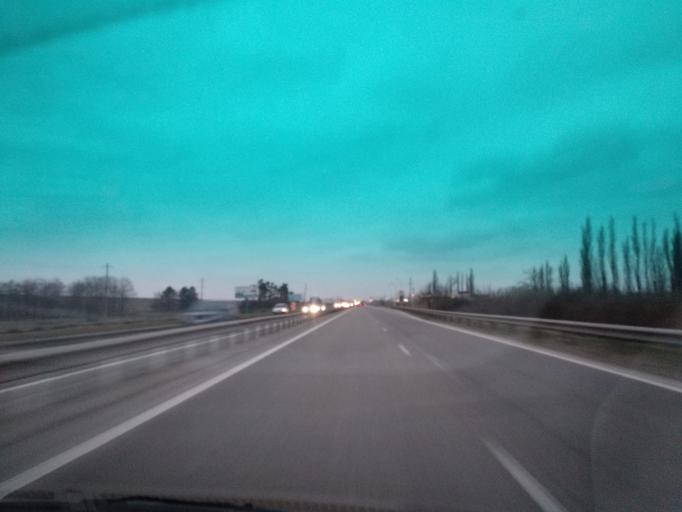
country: RU
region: Adygeya
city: Tlyustenkhabl'
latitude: 44.9293
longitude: 39.1386
